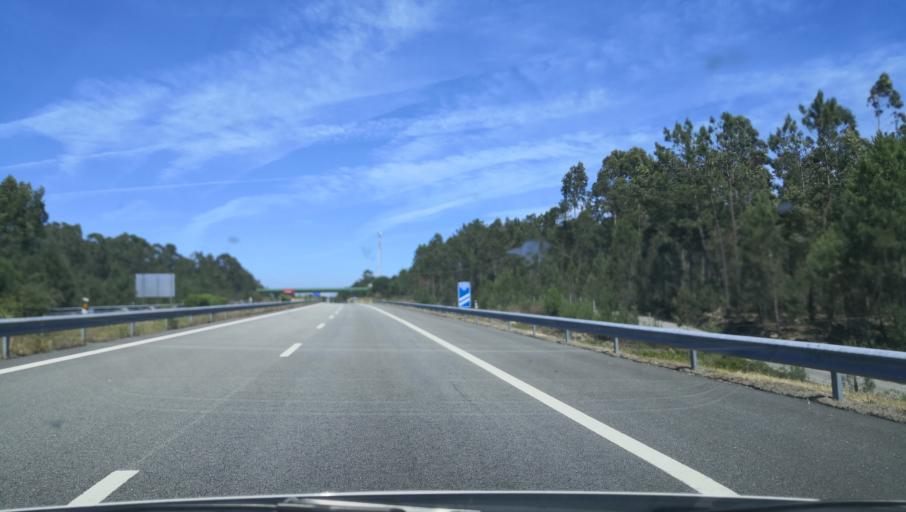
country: PT
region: Coimbra
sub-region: Montemor-O-Velho
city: Arazede
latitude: 40.2550
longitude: -8.6383
